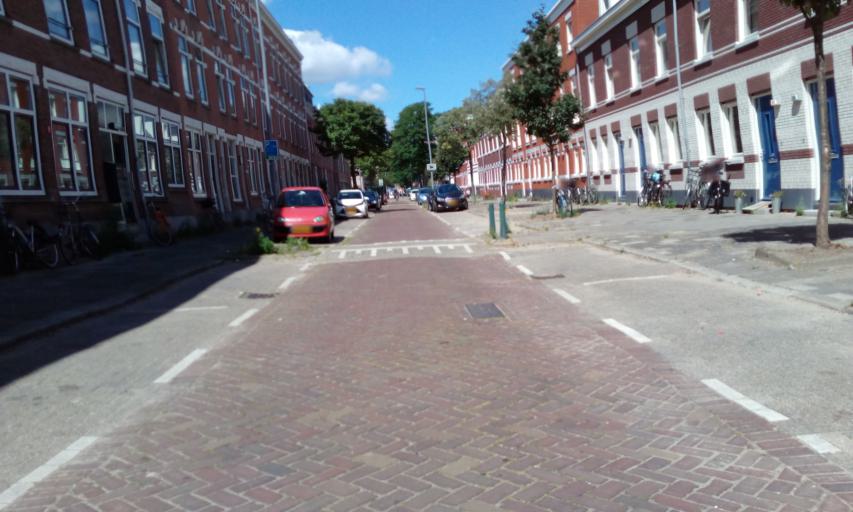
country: NL
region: South Holland
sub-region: Gemeente Rotterdam
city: Rotterdam
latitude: 51.9360
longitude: 4.4842
